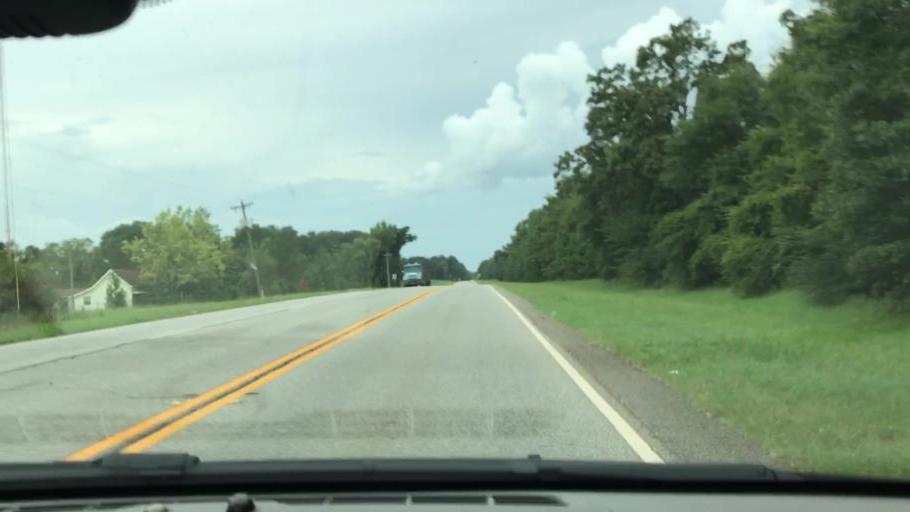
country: US
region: Georgia
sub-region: Early County
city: Blakely
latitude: 31.3006
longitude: -85.0543
